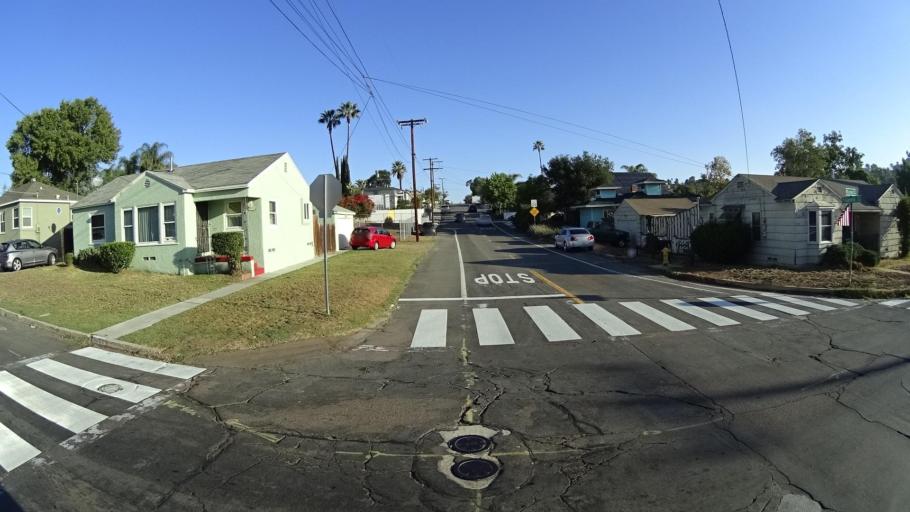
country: US
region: California
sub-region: San Diego County
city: La Mesa
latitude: 32.7683
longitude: -117.0059
